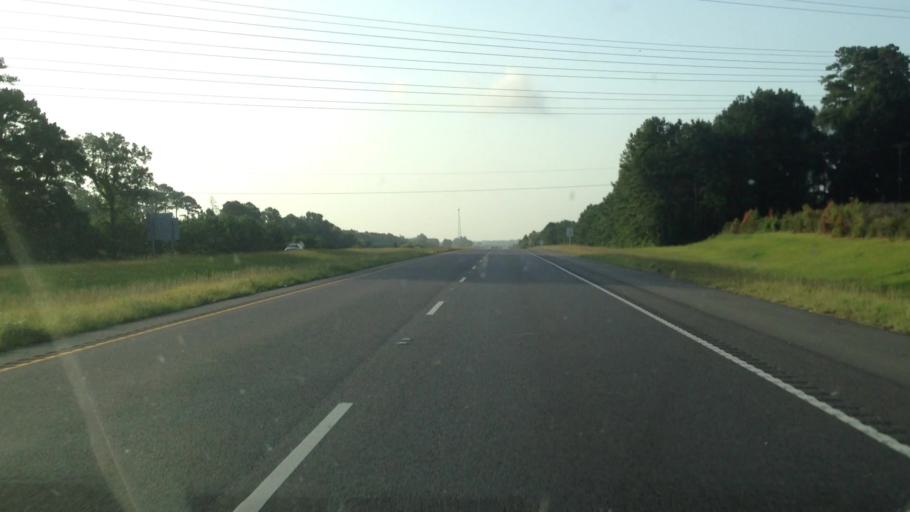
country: US
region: Louisiana
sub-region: Rapides Parish
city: Boyce
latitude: 31.4032
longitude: -92.7082
